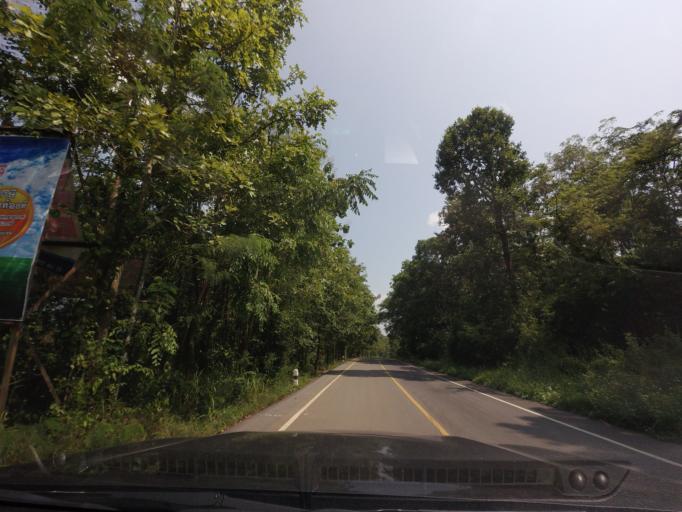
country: TH
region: Nan
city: Nan
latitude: 18.8530
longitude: 100.7857
